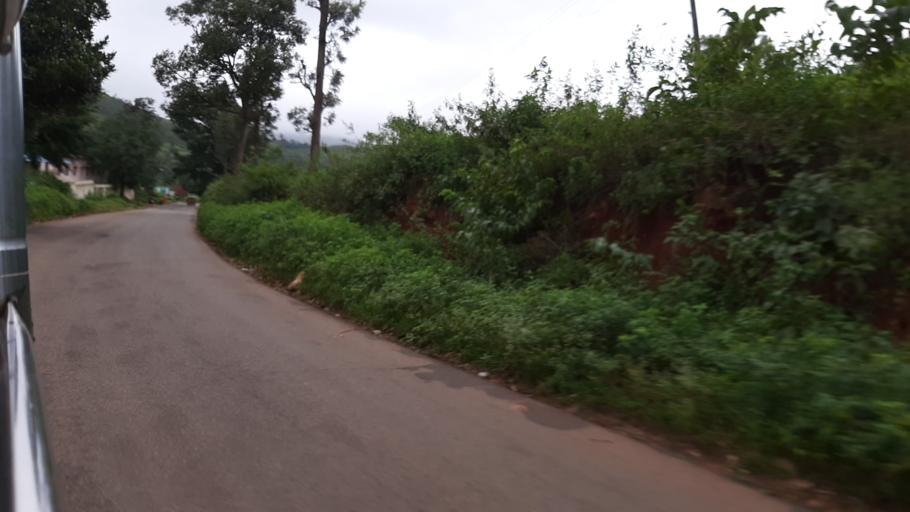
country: IN
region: Andhra Pradesh
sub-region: Vizianagaram District
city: Salur
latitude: 18.2859
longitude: 82.9388
